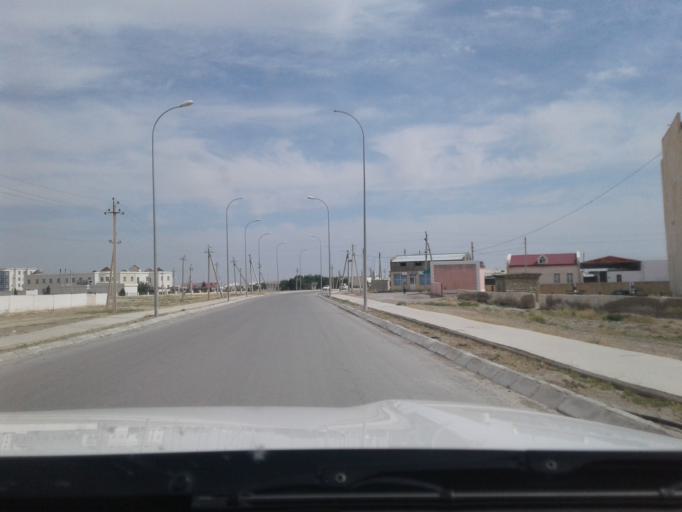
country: TM
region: Balkan
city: Serdar
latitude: 38.9949
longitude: 56.2701
